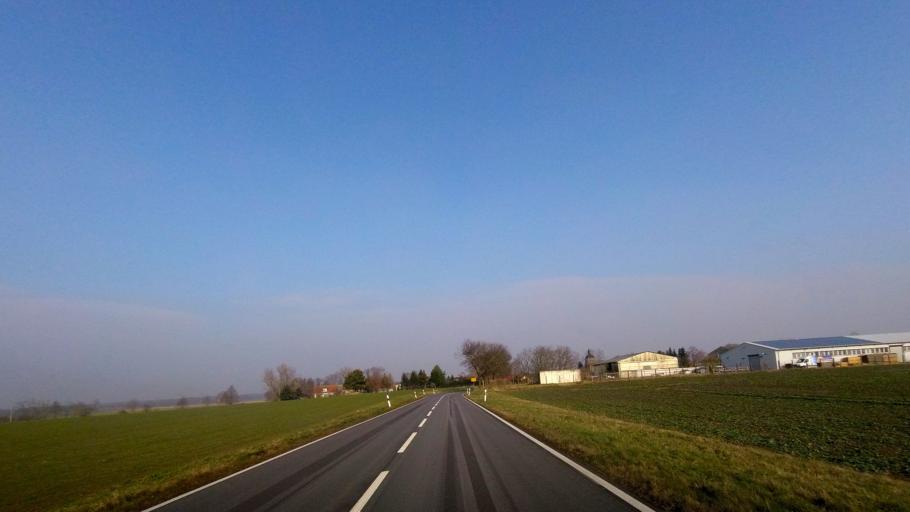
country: DE
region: Brandenburg
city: Juterbog
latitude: 51.9606
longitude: 13.0415
